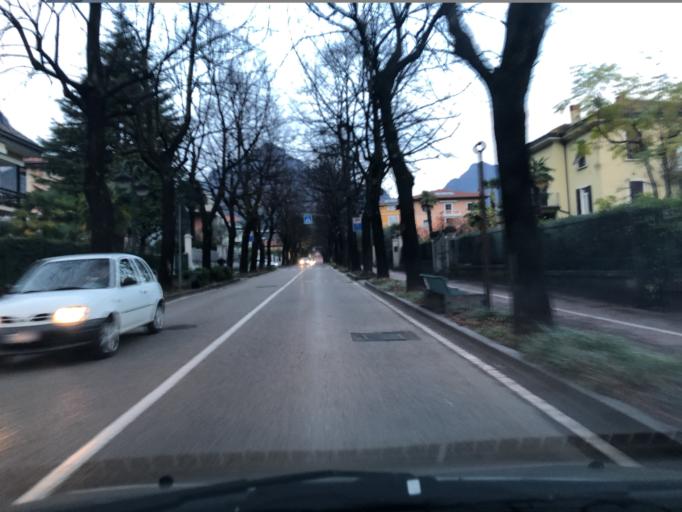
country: IT
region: Trentino-Alto Adige
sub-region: Provincia di Trento
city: Riva del Garda
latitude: 45.8898
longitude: 10.8430
